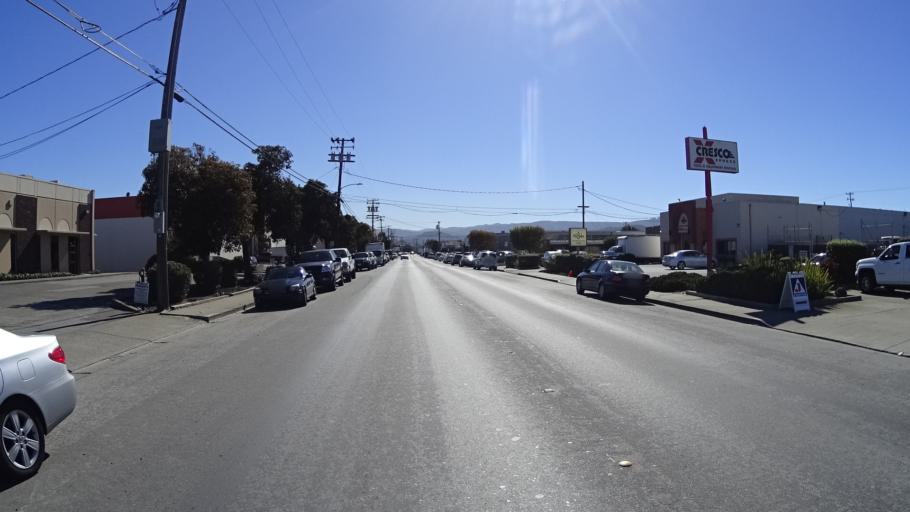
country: US
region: California
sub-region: San Mateo County
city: South San Francisco
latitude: 37.6474
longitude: -122.4095
